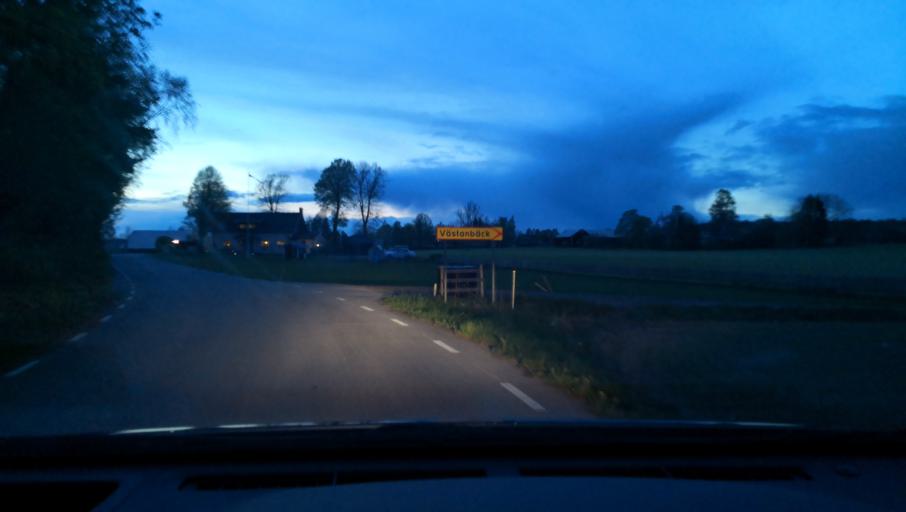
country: SE
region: OErebro
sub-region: Orebro Kommun
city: Vintrosa
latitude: 59.1513
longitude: 15.0057
